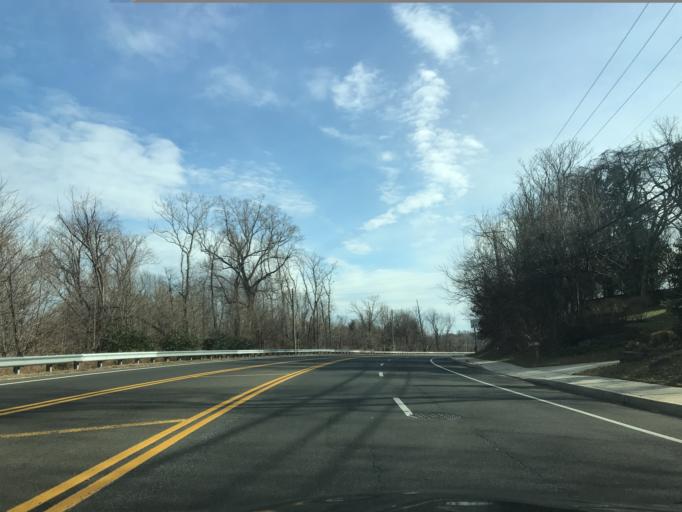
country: US
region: Maryland
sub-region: Prince George's County
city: Woodmore
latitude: 38.9243
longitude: -76.8042
